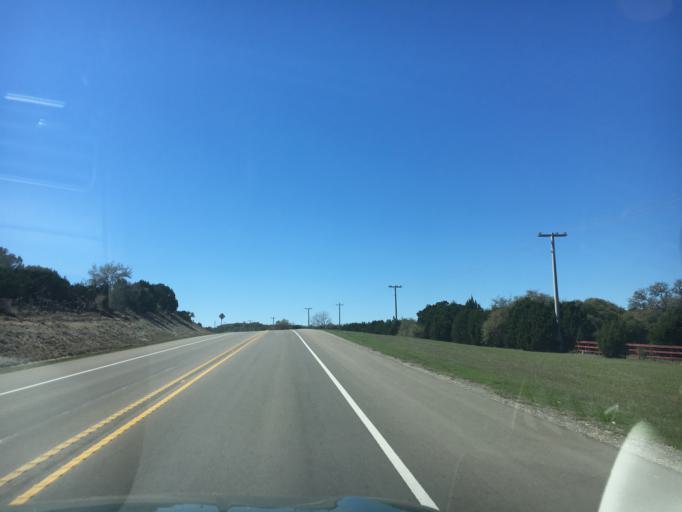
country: US
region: Texas
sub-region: Travis County
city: The Hills
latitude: 30.2873
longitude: -98.0539
